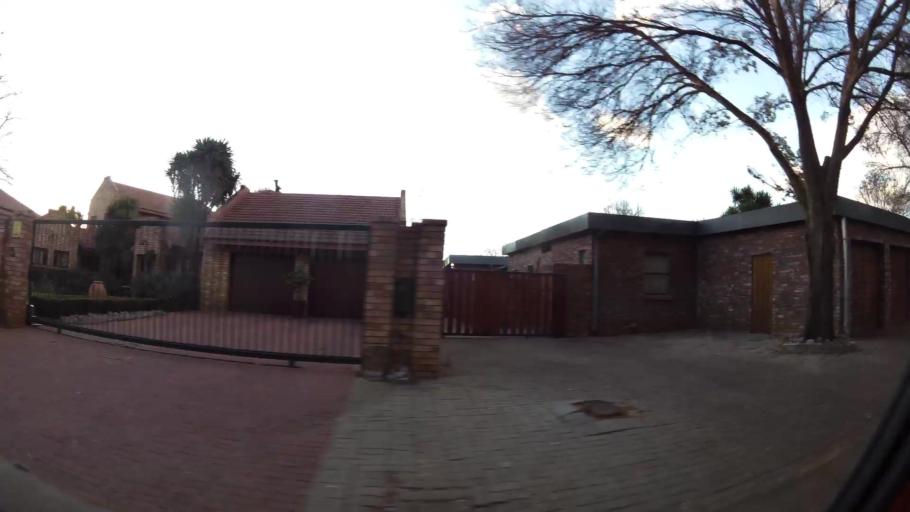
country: ZA
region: North-West
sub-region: Dr Kenneth Kaunda District Municipality
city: Potchefstroom
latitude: -26.6794
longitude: 27.1078
